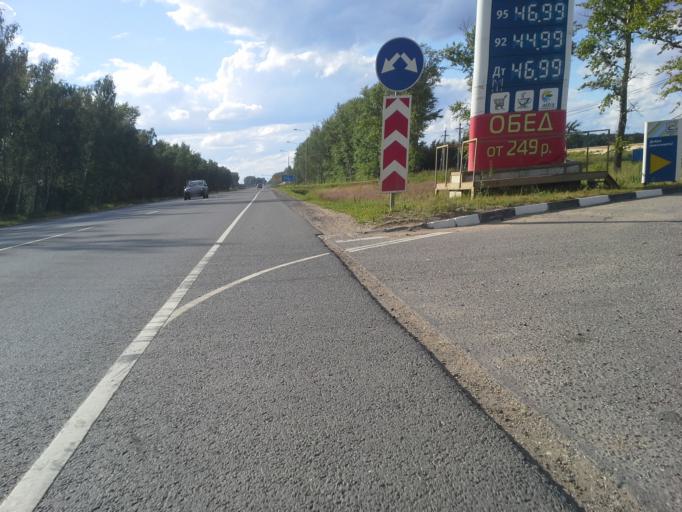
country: RU
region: Moskovskaya
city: L'vovskiy
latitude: 55.3439
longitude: 37.4578
